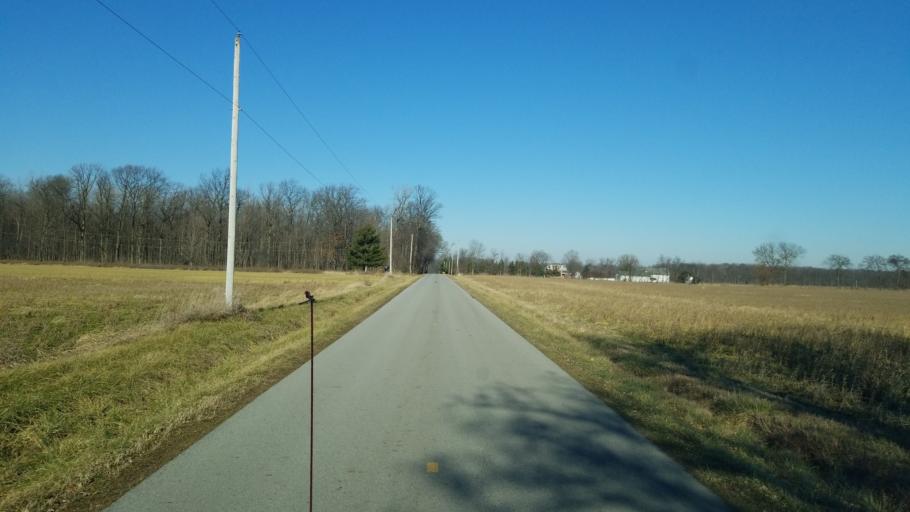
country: US
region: Ohio
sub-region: Henry County
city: Liberty Center
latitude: 41.4097
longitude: -83.9707
